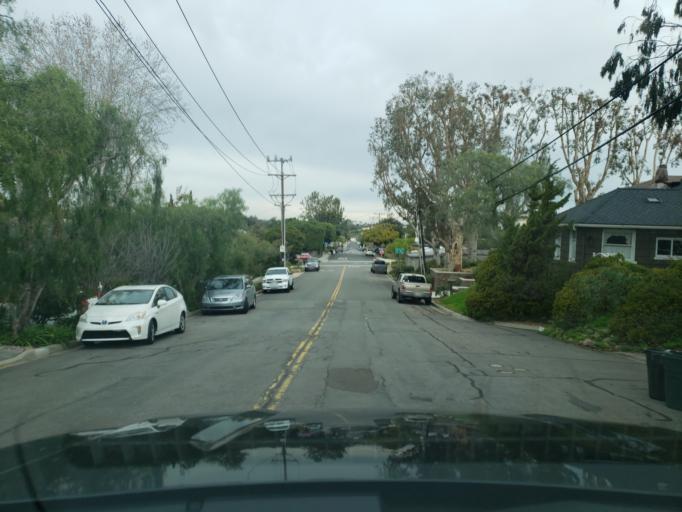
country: US
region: California
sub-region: San Diego County
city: Coronado
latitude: 32.7210
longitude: -117.2421
